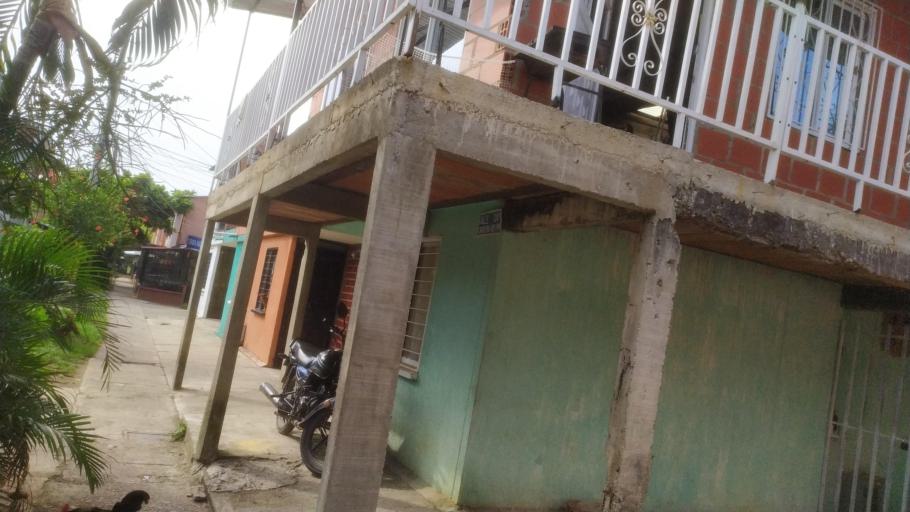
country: CO
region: Valle del Cauca
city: Jamundi
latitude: 3.2390
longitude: -76.5077
